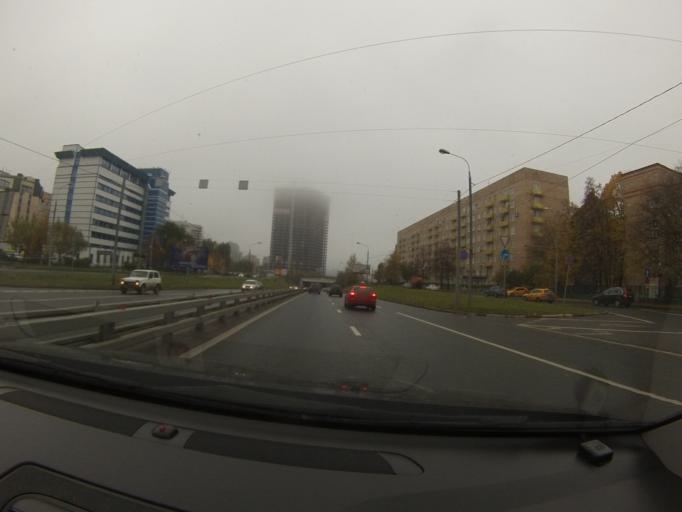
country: RU
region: Moskovskaya
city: Kastanayevo
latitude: 55.7087
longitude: 37.5093
